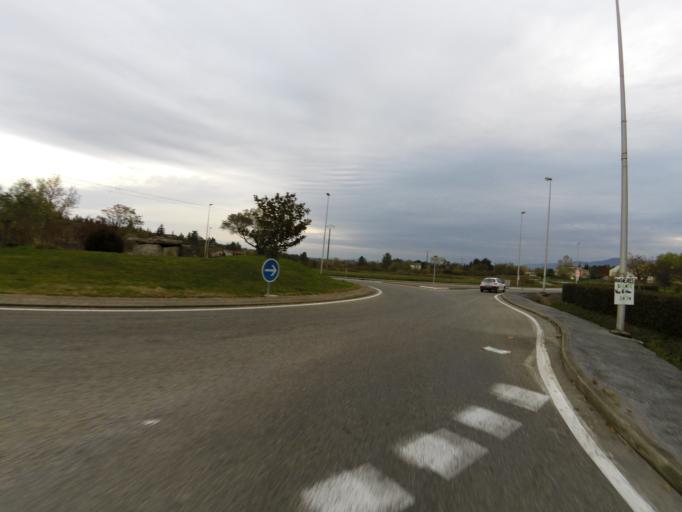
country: FR
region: Rhone-Alpes
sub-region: Departement de l'Ardeche
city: Lablachere
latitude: 44.4602
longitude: 4.2183
